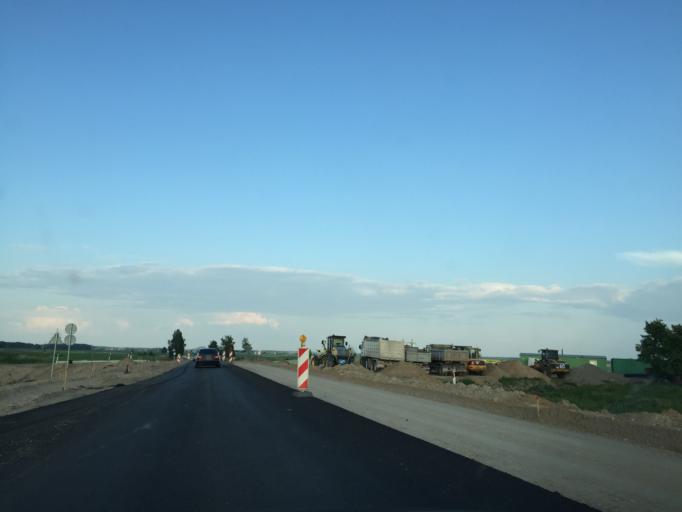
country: LT
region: Telsiu apskritis
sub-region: Telsiai
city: Telsiai
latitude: 56.0050
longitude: 22.3028
